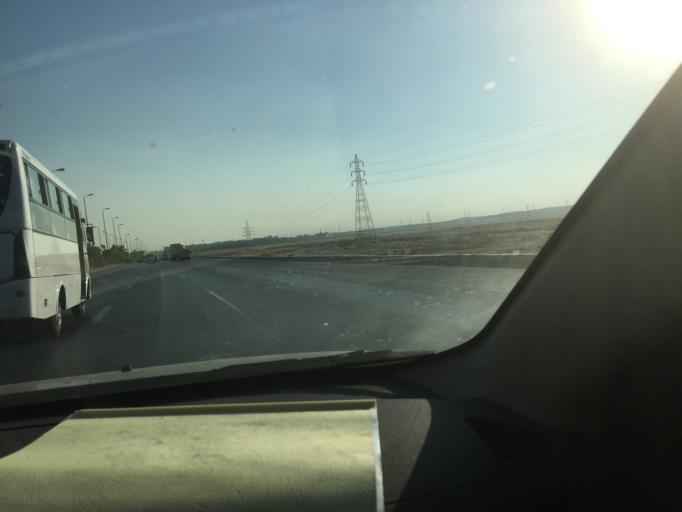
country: EG
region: Eastern Province
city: Bilbays
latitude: 30.2562
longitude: 31.7423
